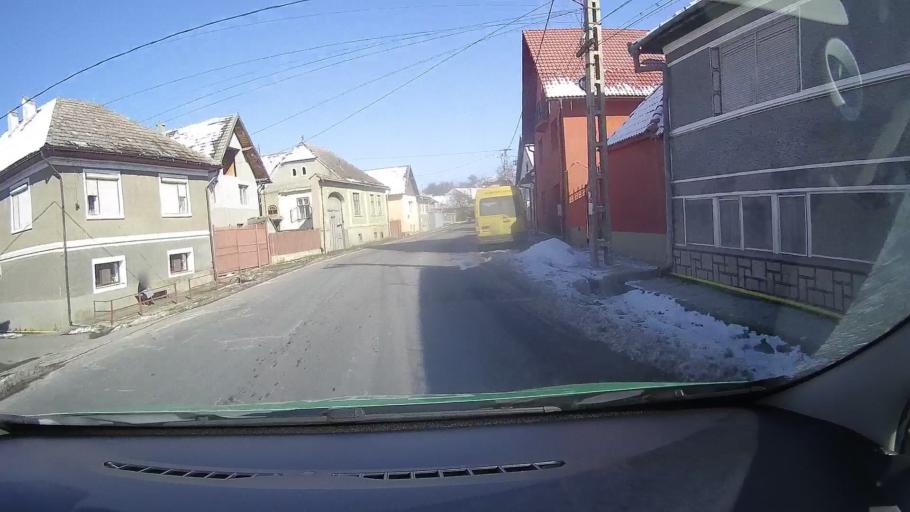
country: RO
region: Brasov
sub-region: Comuna Hoghiz
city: Hoghiz
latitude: 45.9640
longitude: 25.2969
